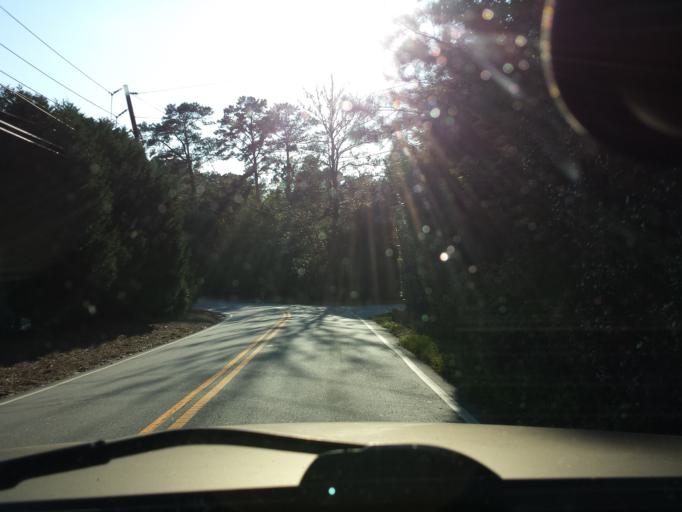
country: US
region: Georgia
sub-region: Cobb County
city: Vinings
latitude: 33.8708
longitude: -84.4243
